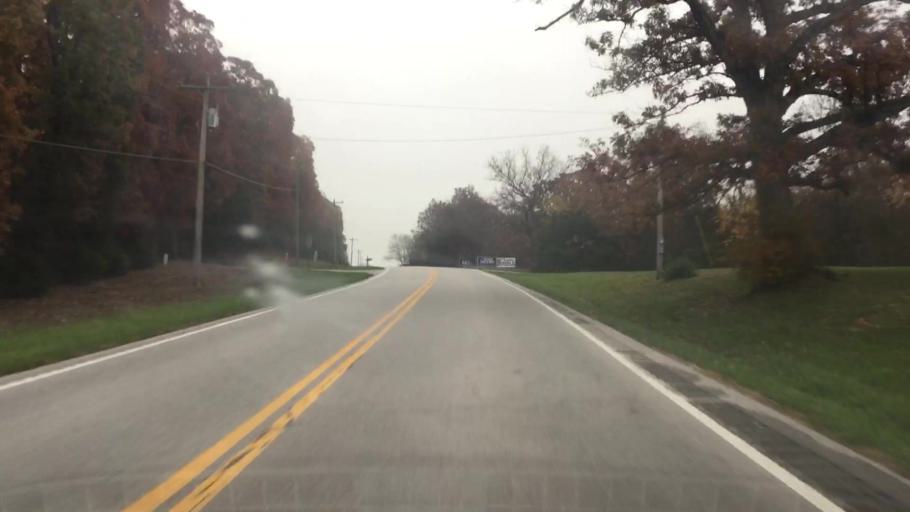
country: US
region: Missouri
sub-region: Callaway County
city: Fulton
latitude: 38.8757
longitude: -92.0716
